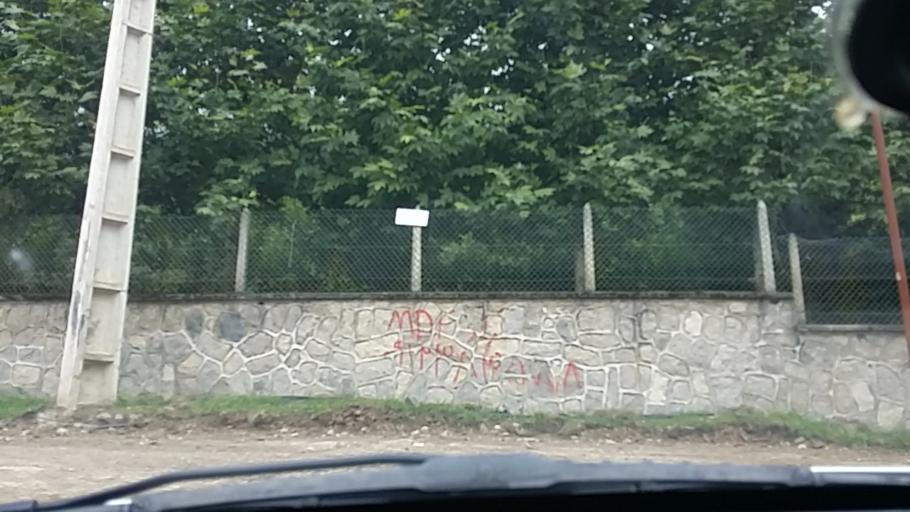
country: IR
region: Mazandaran
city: `Abbasabad
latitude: 36.4894
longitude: 51.1672
